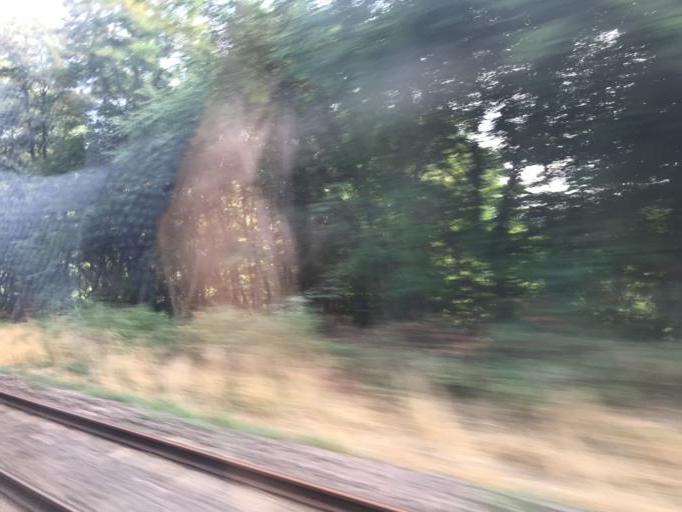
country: DE
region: Saarland
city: Namborn
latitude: 49.5182
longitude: 7.1448
